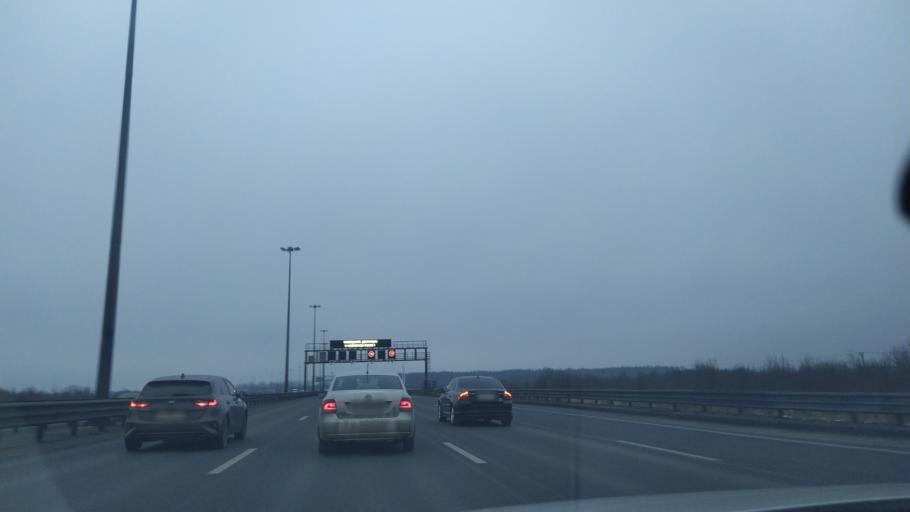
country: RU
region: St.-Petersburg
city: Krasnogvargeisky
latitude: 60.0039
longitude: 30.4762
